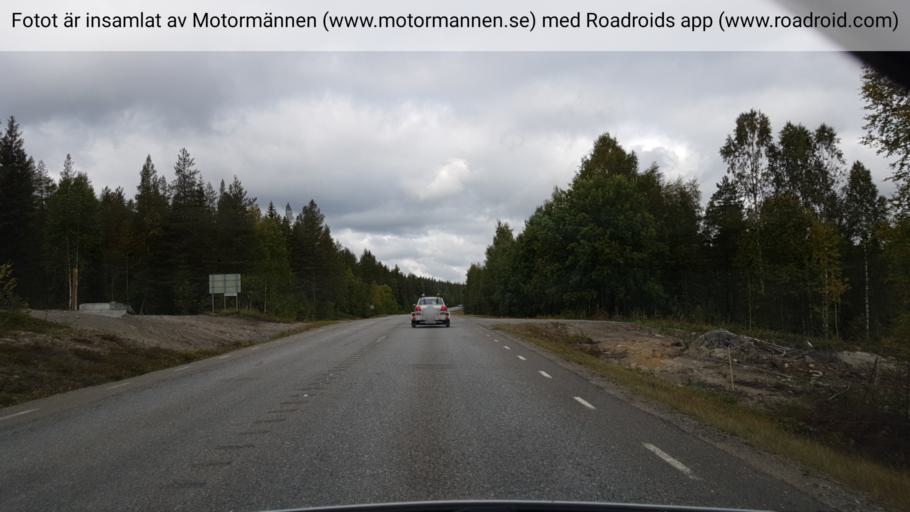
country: SE
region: Vaesterbotten
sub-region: Skelleftea Kommun
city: Boliden
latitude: 64.8841
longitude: 20.3868
